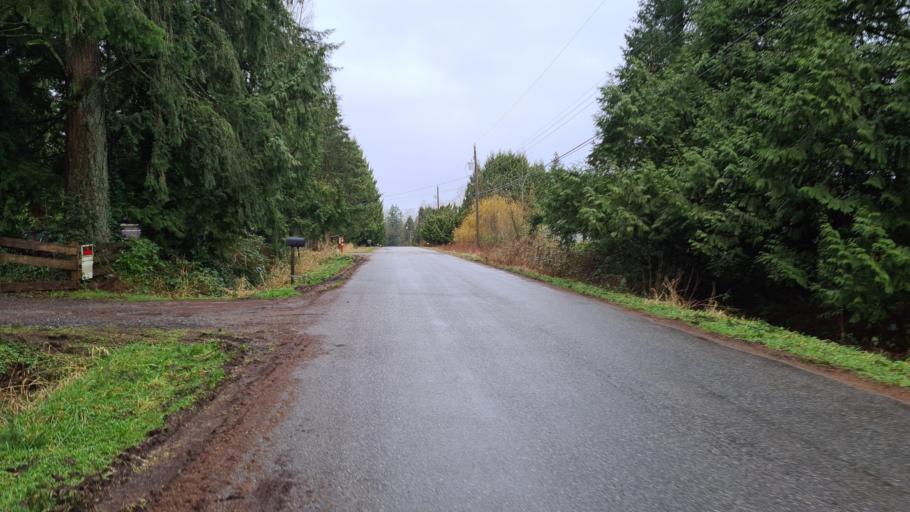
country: CA
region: British Columbia
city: Walnut Grove
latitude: 49.1383
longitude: -122.6544
